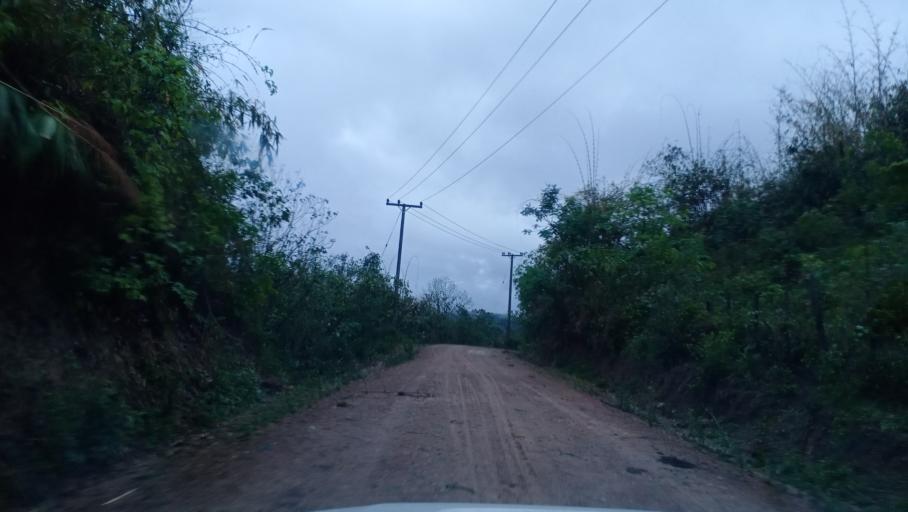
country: VN
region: Huyen Dien Bien
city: Dien Bien Phu
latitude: 21.3273
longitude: 102.7157
